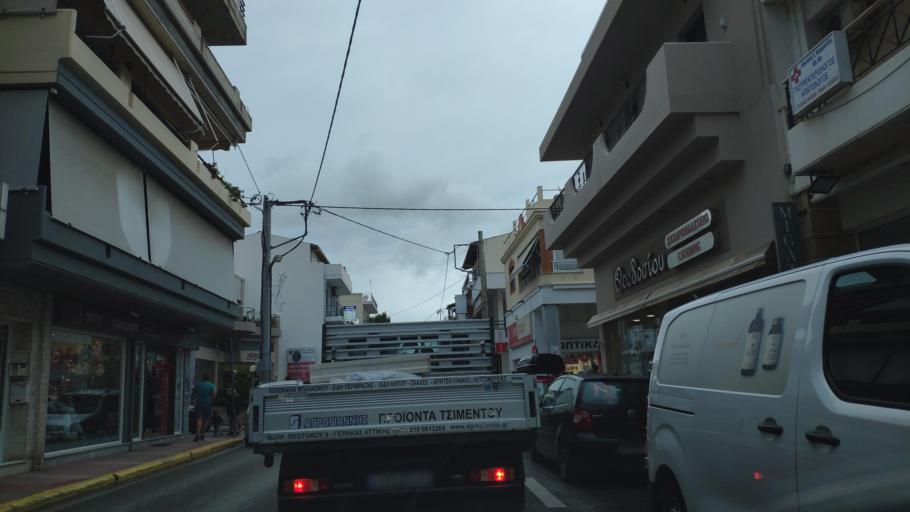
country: GR
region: Attica
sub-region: Nomarchia Anatolikis Attikis
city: Artemida
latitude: 37.9737
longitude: 24.0084
